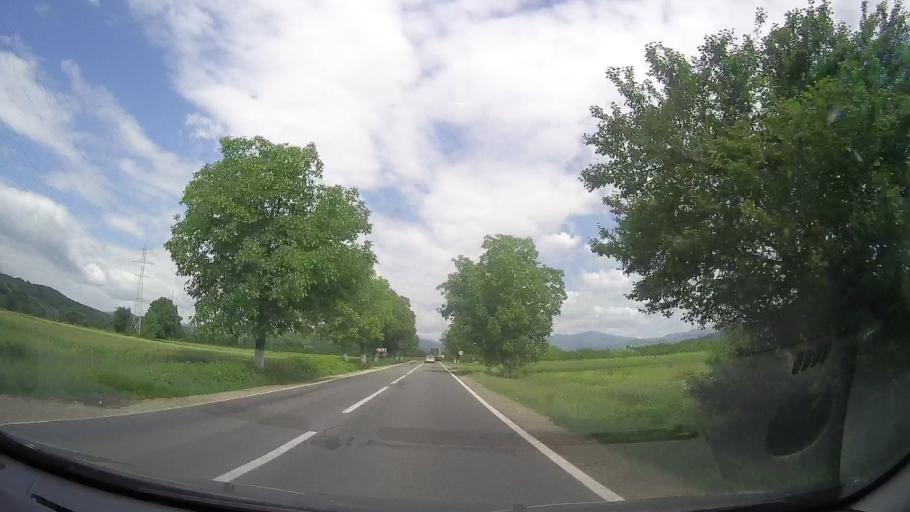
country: RO
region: Prahova
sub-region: Comuna Izvoarele
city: Homoraciu
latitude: 45.2457
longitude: 26.0248
